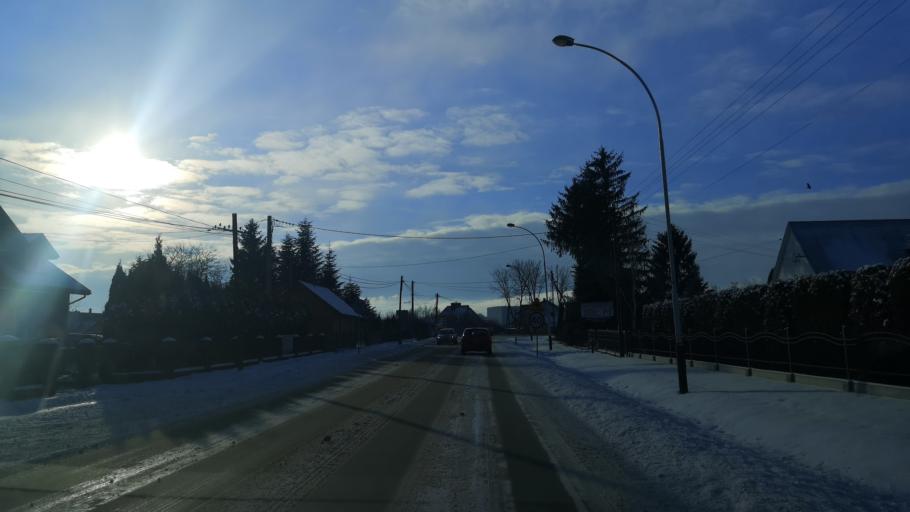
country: PL
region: Subcarpathian Voivodeship
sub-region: Powiat przeworski
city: Przeworsk
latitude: 50.0753
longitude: 22.4936
